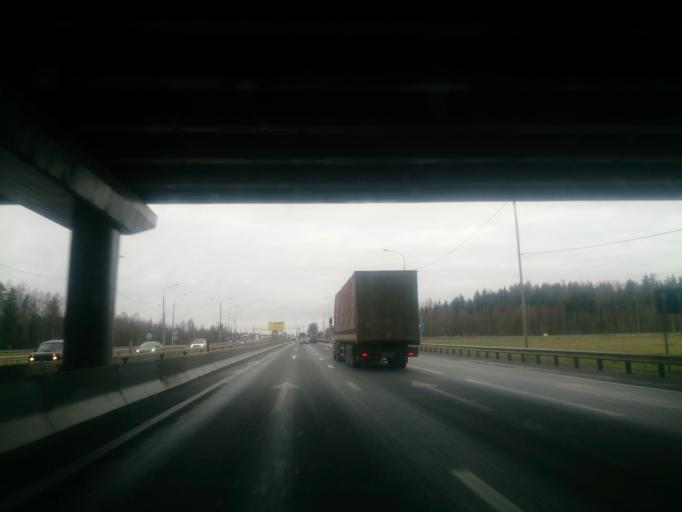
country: RU
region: Leningrad
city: Ul'yanovka
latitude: 59.6056
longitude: 30.7592
